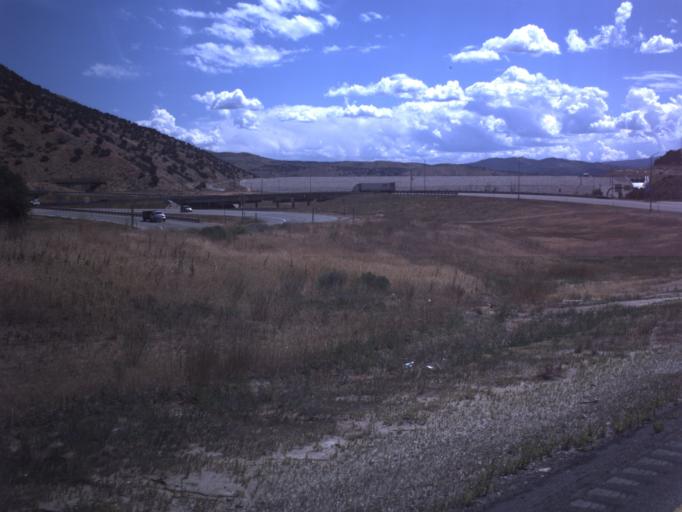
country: US
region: Utah
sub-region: Summit County
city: Coalville
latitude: 40.9720
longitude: -111.4427
